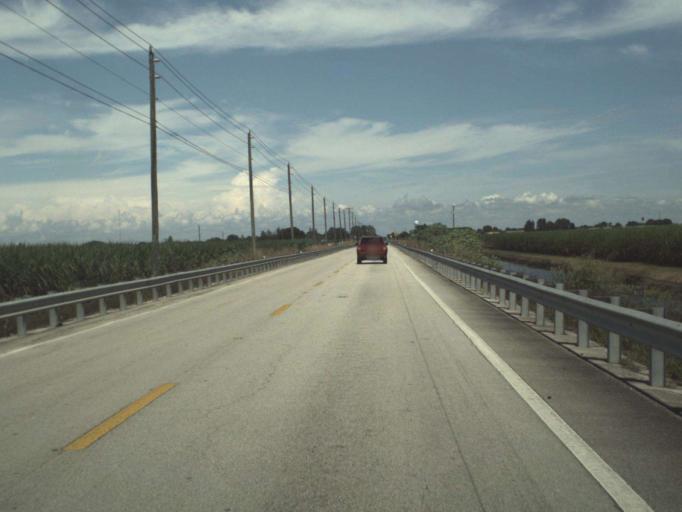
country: US
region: Florida
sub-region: Palm Beach County
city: Pahokee
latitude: 26.7953
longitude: -80.6533
